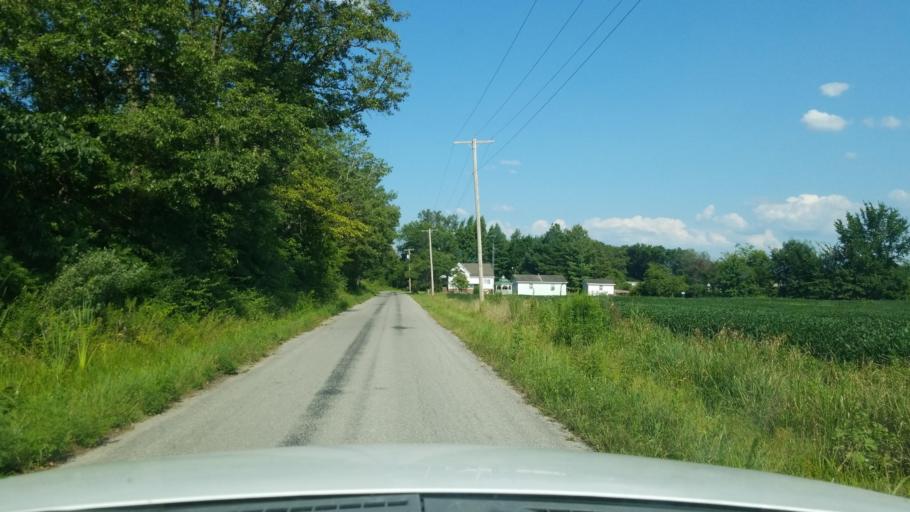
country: US
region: Illinois
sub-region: Saline County
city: Eldorado
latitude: 37.7863
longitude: -88.4913
